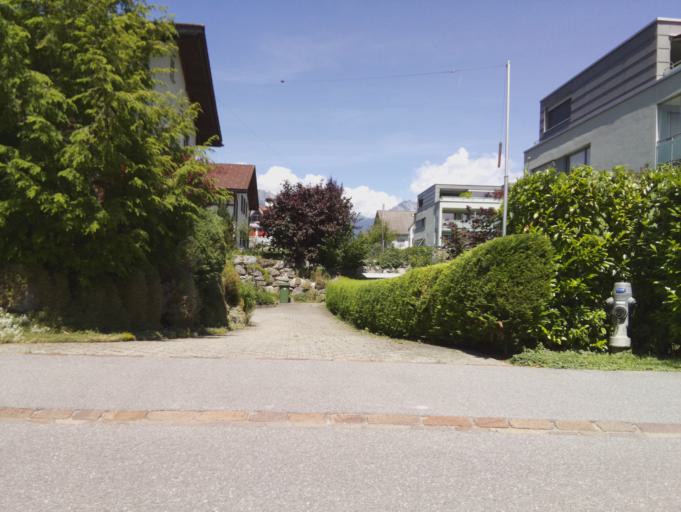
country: CH
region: Glarus
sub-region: Glarus
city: Nafels
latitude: 47.0896
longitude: 9.0628
